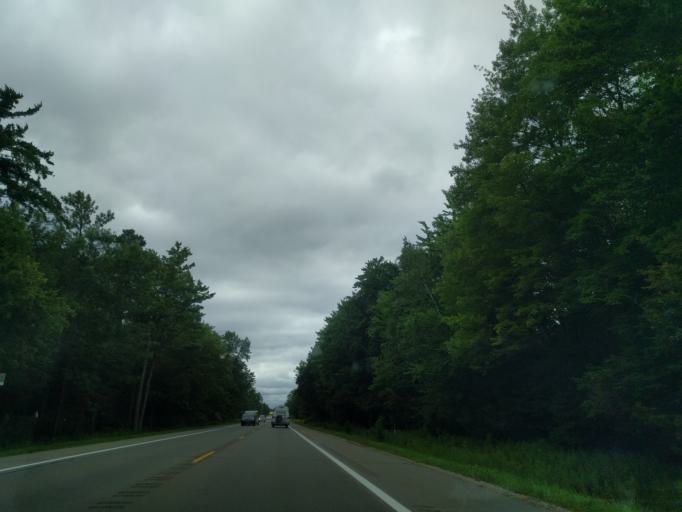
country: US
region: Michigan
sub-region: Menominee County
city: Menominee
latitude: 45.3191
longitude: -87.4319
